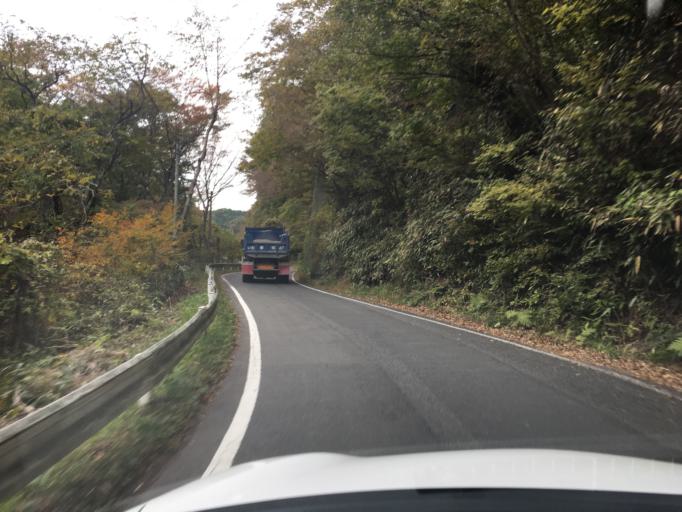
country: JP
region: Fukushima
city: Iwaki
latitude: 37.1988
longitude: 140.7794
